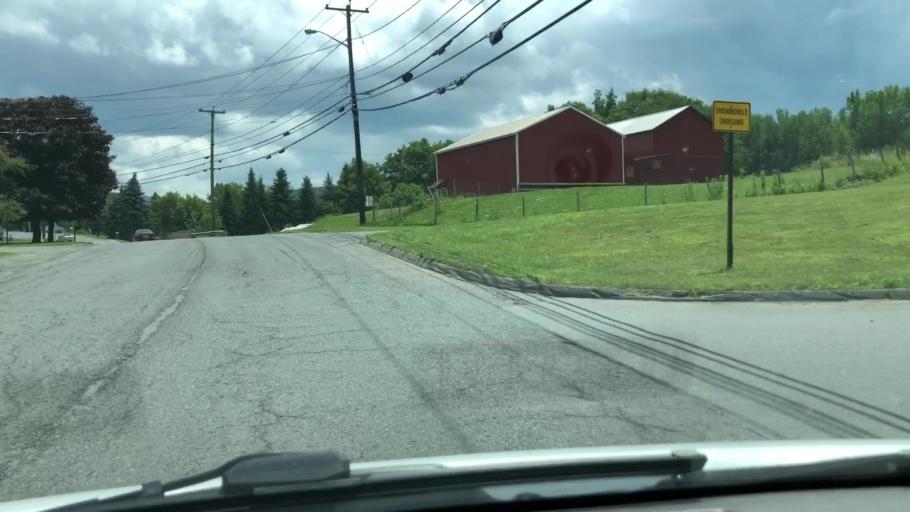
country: US
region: Massachusetts
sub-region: Berkshire County
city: Adams
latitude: 42.5898
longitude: -73.1137
